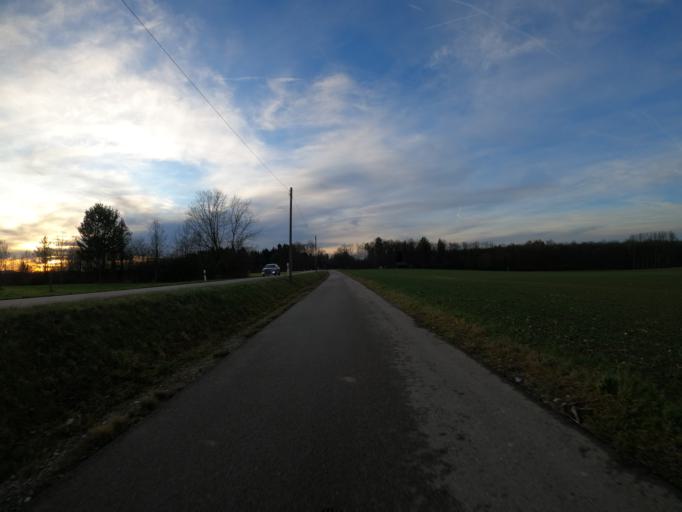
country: DE
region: Baden-Wuerttemberg
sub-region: Regierungsbezirk Stuttgart
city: Hattenhofen
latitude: 48.6664
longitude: 9.5499
